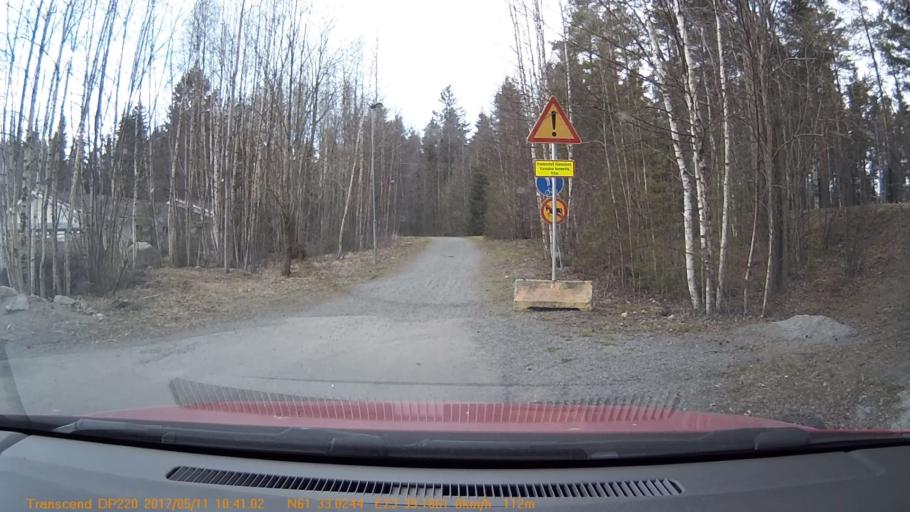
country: FI
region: Pirkanmaa
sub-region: Tampere
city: Yloejaervi
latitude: 61.5504
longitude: 23.6528
